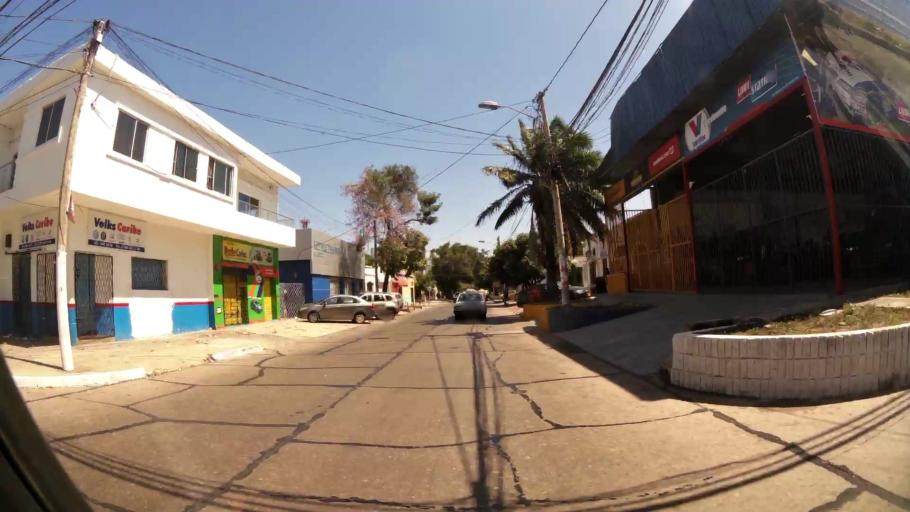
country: CO
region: Atlantico
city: Barranquilla
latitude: 10.9896
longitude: -74.7966
